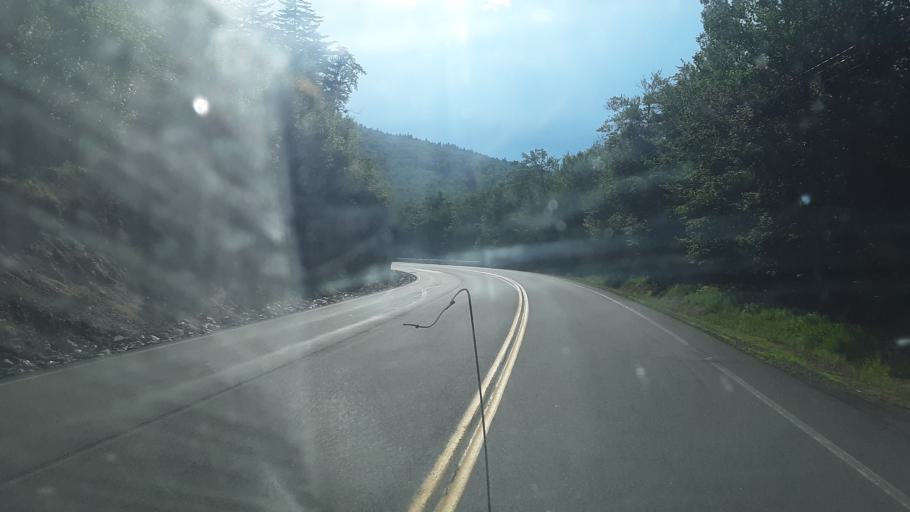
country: US
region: Maine
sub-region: Washington County
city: Calais
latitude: 45.4549
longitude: -67.7437
